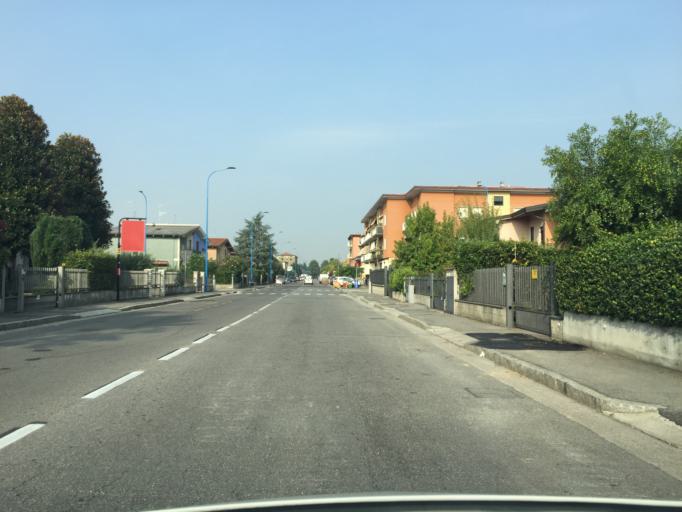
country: IT
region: Lombardy
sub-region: Provincia di Brescia
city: Folzano
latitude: 45.5074
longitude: 10.1911
